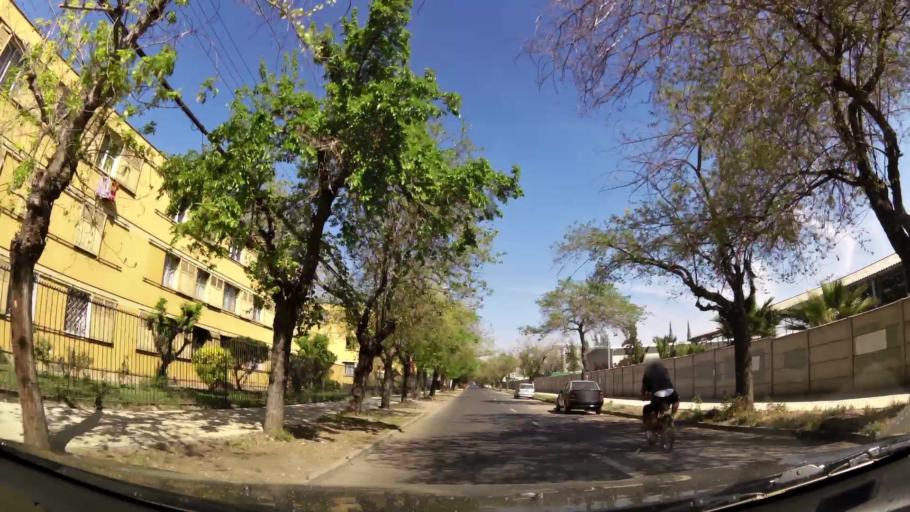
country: CL
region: Santiago Metropolitan
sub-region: Provincia de Santiago
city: Santiago
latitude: -33.4240
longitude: -70.6596
